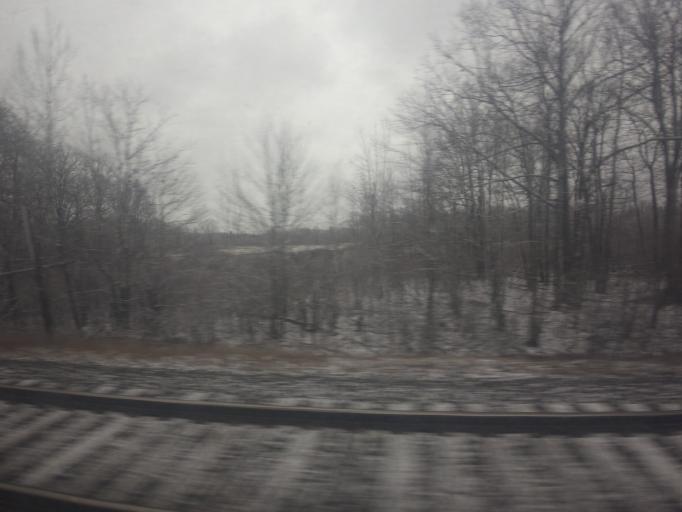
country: US
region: New York
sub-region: Jefferson County
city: Alexandria Bay
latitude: 44.4279
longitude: -75.9762
